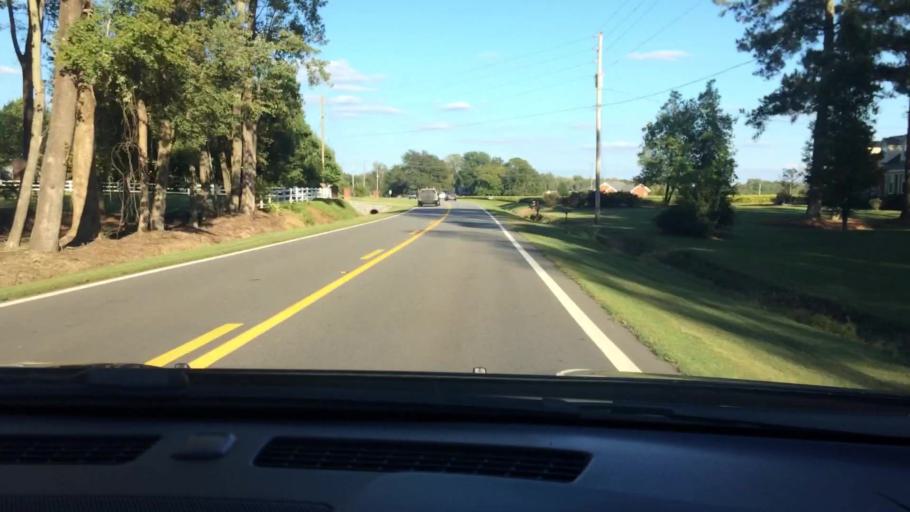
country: US
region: North Carolina
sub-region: Pitt County
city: Winterville
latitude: 35.5199
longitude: -77.4367
